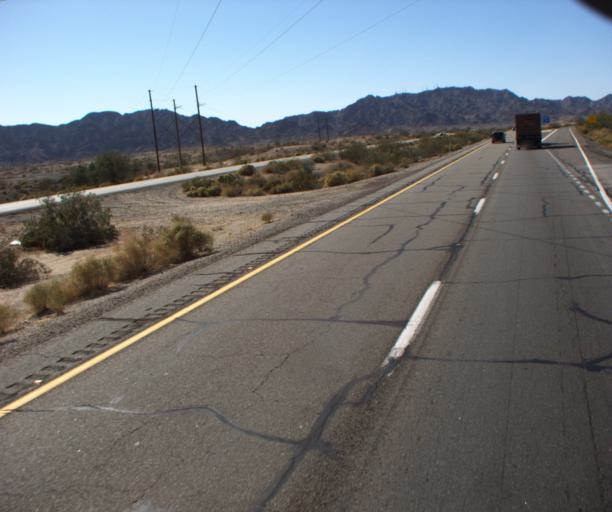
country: US
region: Arizona
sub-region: Yuma County
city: Wellton
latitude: 32.6656
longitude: -114.2769
